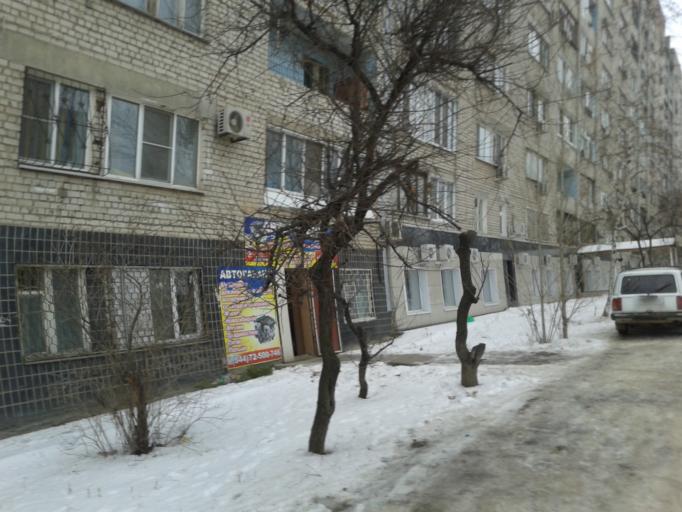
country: RU
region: Volgograd
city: Volgograd
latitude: 48.7273
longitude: 44.5223
